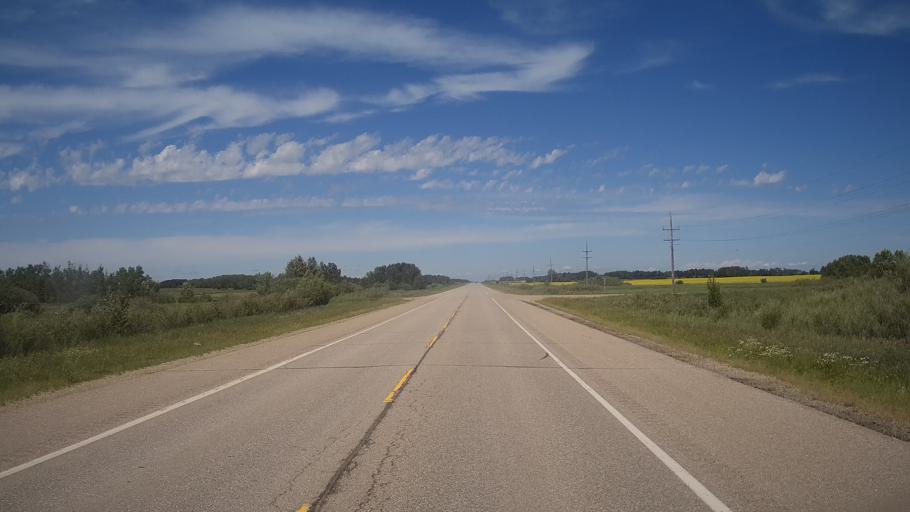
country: CA
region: Saskatchewan
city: Langenburg
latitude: 50.6520
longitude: -101.2760
